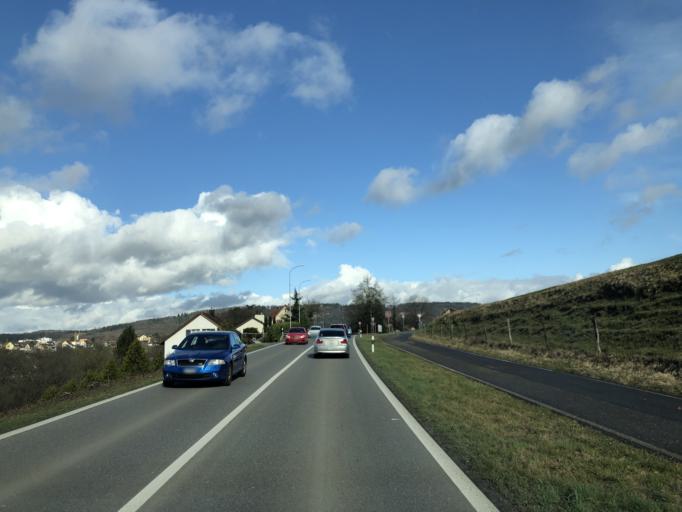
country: CH
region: Aargau
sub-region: Bezirk Baden
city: Gebenstorf
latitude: 47.4740
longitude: 8.2325
